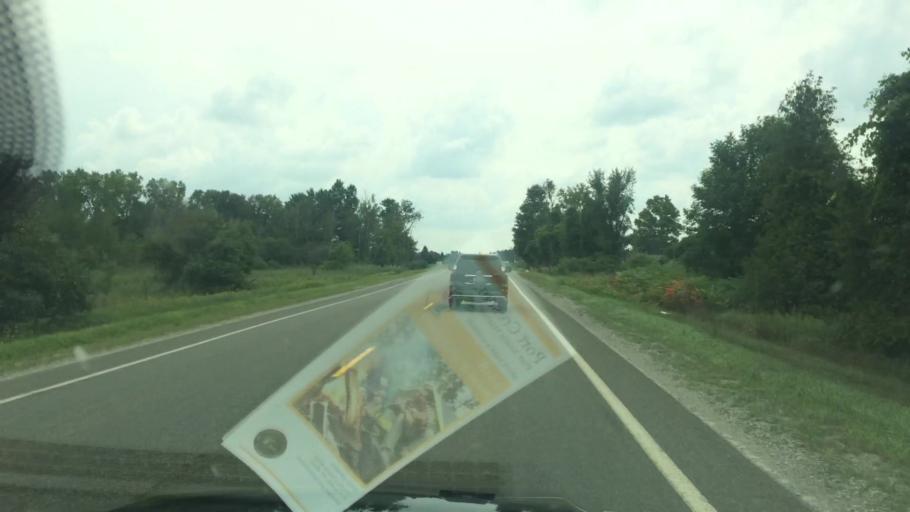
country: US
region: Michigan
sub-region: Tuscola County
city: Cass City
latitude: 43.6730
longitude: -83.0983
